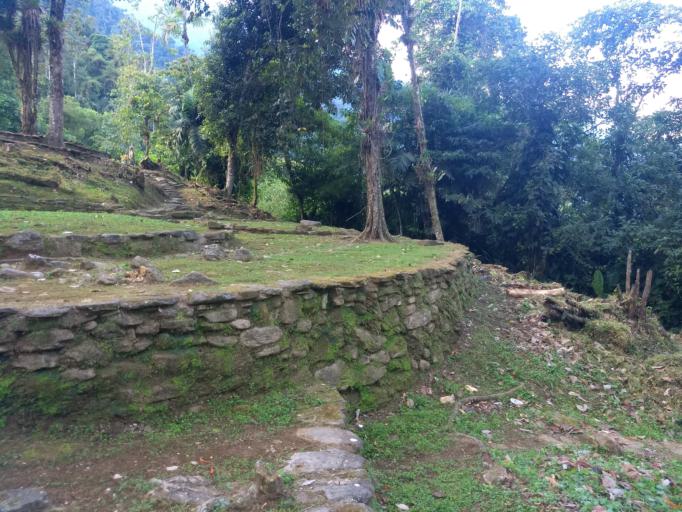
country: CO
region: Magdalena
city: Cienaga
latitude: 11.0419
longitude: -73.9244
